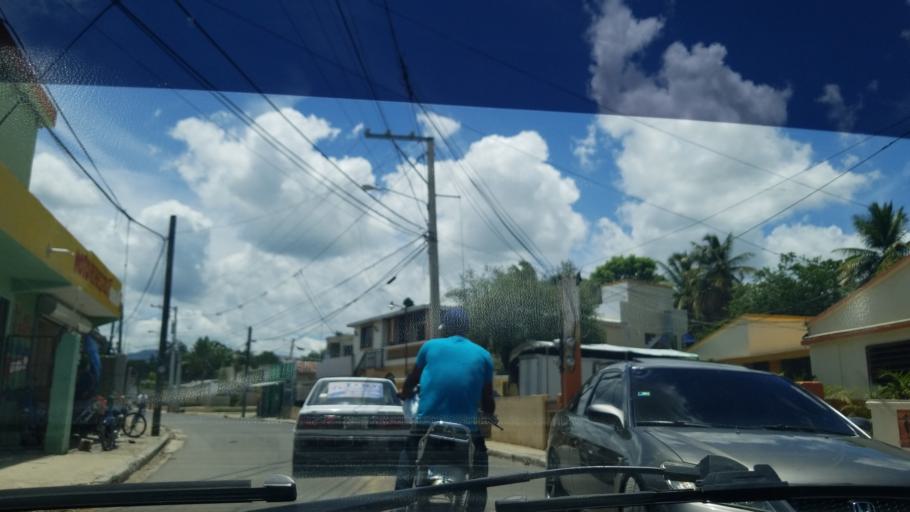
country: DO
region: Santiago
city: Santiago de los Caballeros
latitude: 19.4796
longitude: -70.6831
